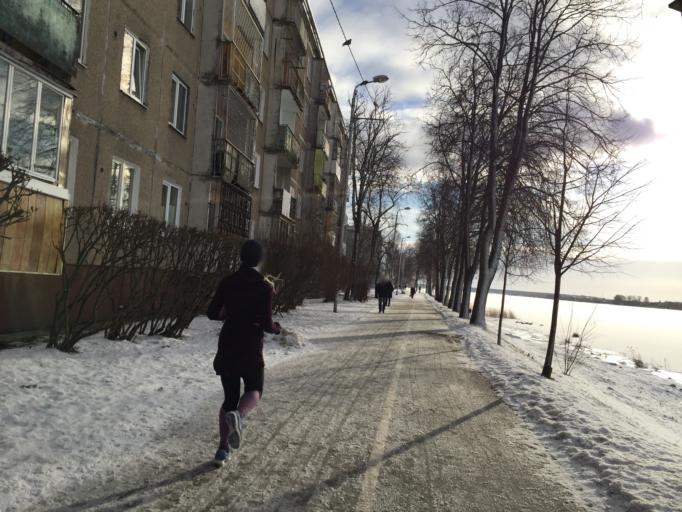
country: LV
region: Kekava
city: Balozi
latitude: 56.9101
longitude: 24.1748
